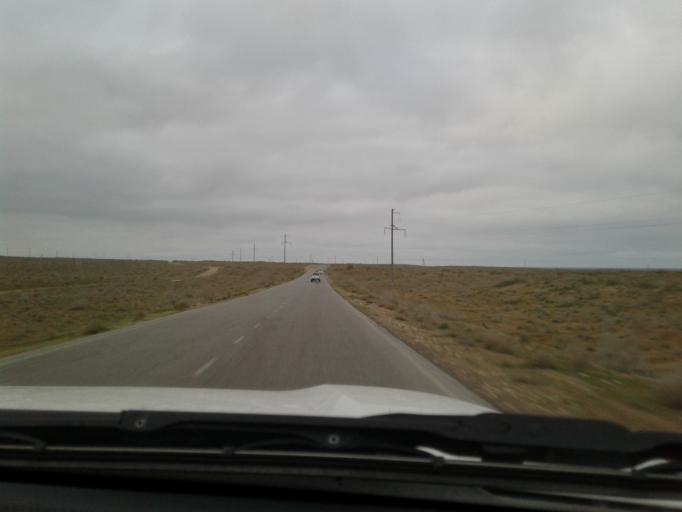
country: TM
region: Lebap
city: Farap
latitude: 39.0913
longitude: 63.7216
